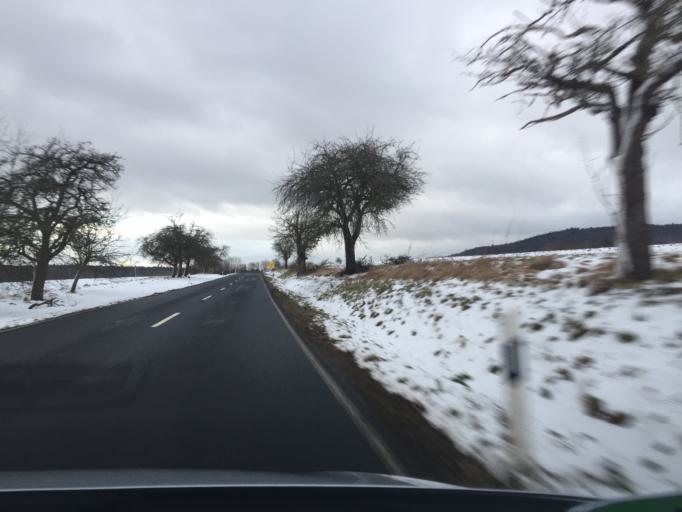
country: DE
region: Bavaria
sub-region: Regierungsbezirk Unterfranken
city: Geiselbach
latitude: 50.1161
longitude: 9.2051
